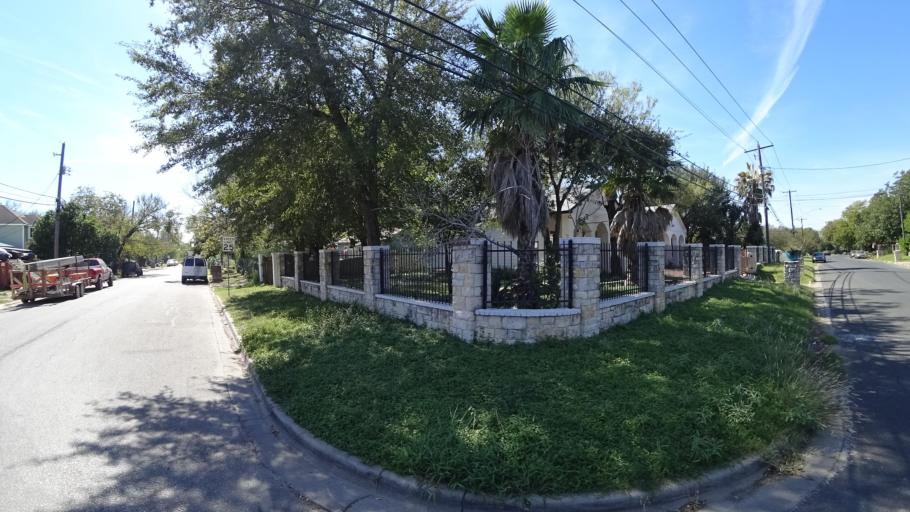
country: US
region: Texas
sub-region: Travis County
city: Austin
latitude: 30.2689
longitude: -97.6797
